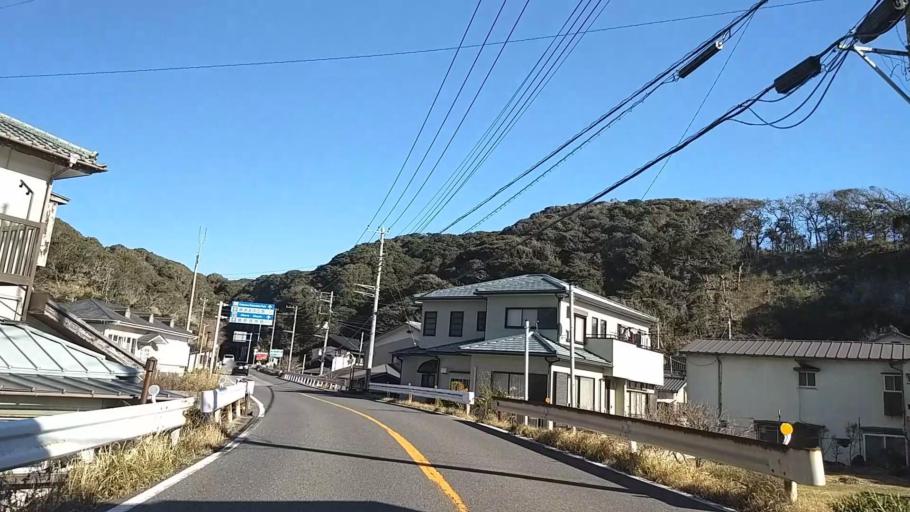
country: JP
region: Chiba
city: Katsuura
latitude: 35.1395
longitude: 140.2739
